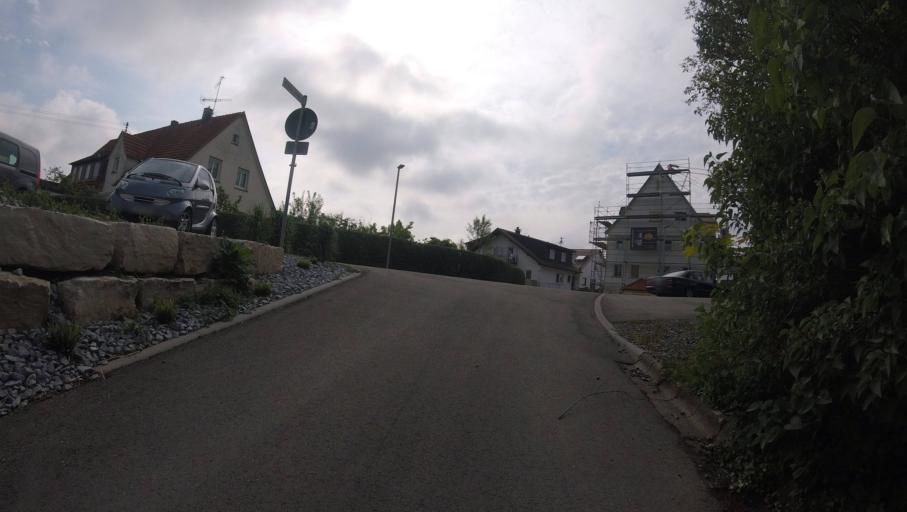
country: DE
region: Baden-Wuerttemberg
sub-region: Regierungsbezirk Stuttgart
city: Rudersberg
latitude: 48.9367
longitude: 9.5178
